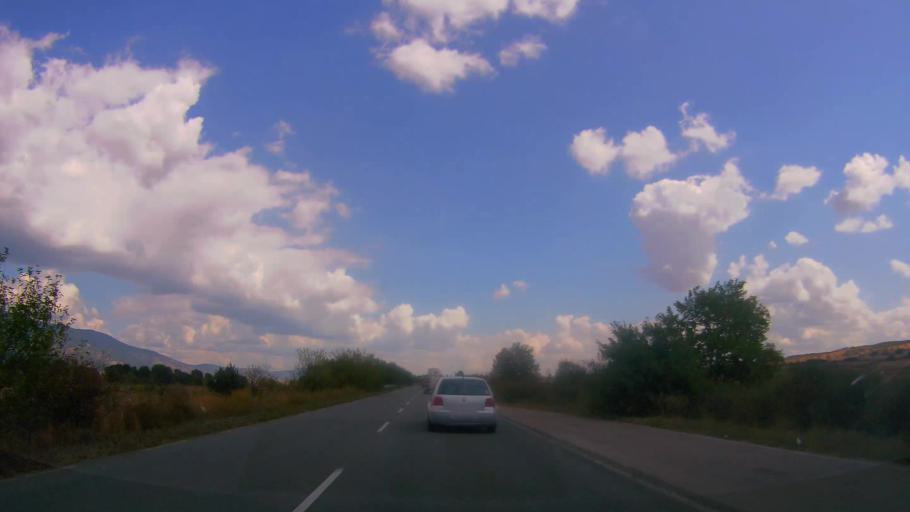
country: BG
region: Sliven
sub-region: Obshtina Tvurditsa
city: Tvurditsa
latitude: 42.6573
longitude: 25.9127
